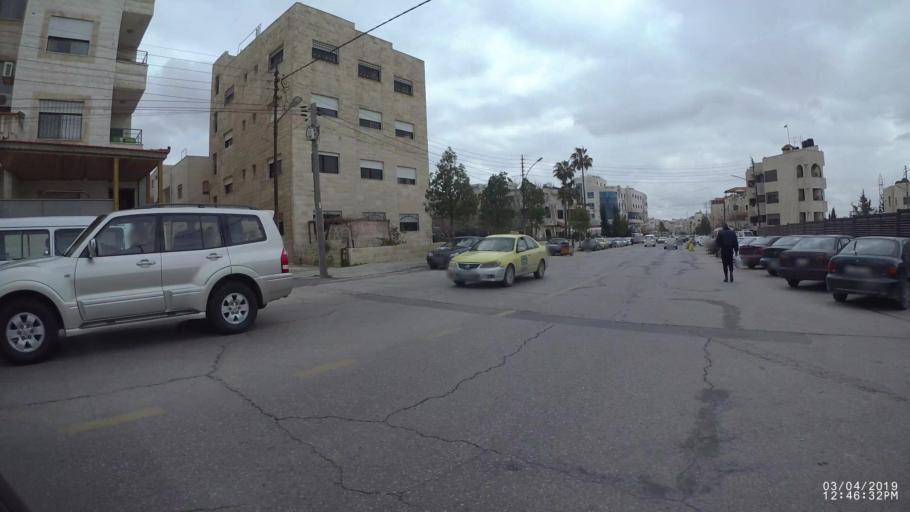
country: JO
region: Amman
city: Wadi as Sir
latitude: 31.9653
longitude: 35.8340
